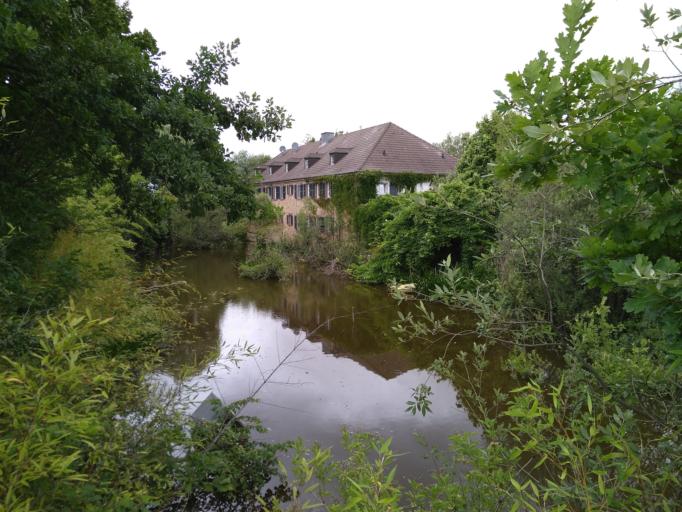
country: DE
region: North Rhine-Westphalia
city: Zulpich
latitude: 50.6612
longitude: 6.6566
